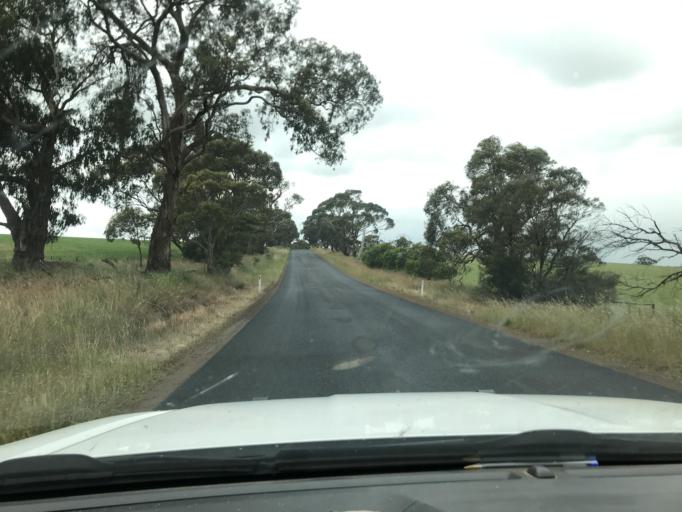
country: AU
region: Victoria
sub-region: Southern Grampians
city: Hamilton
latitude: -37.1821
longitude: 141.5638
